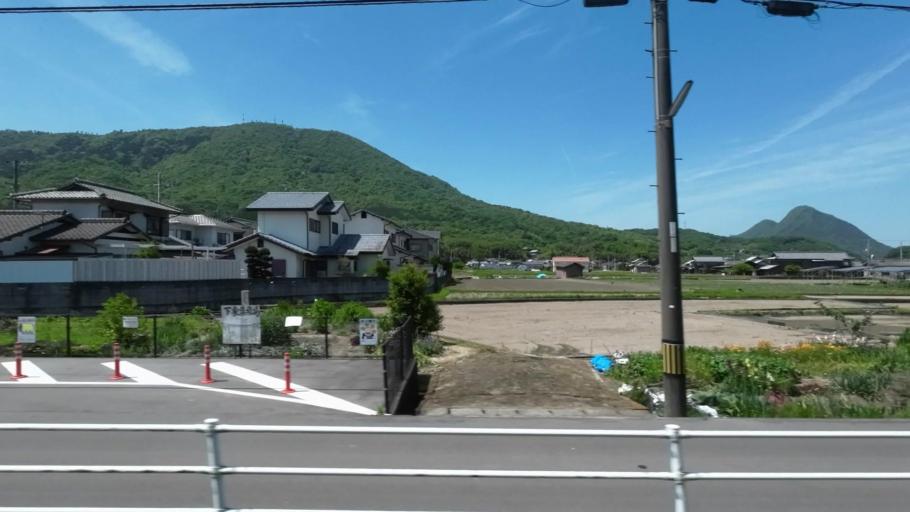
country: JP
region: Kagawa
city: Marugame
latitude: 34.2137
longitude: 133.8010
